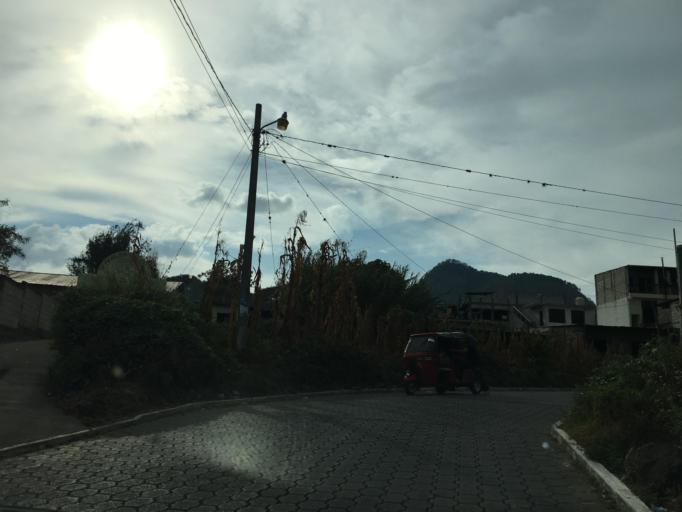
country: GT
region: Solola
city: San Antonio Palopo
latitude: 14.6653
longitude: -91.1639
